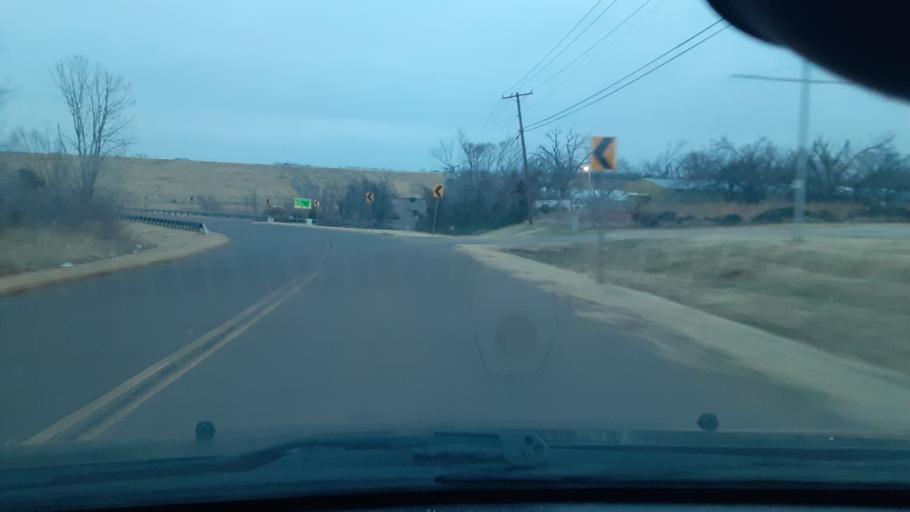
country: US
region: Oklahoma
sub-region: Logan County
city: Guthrie
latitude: 35.8562
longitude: -97.4247
